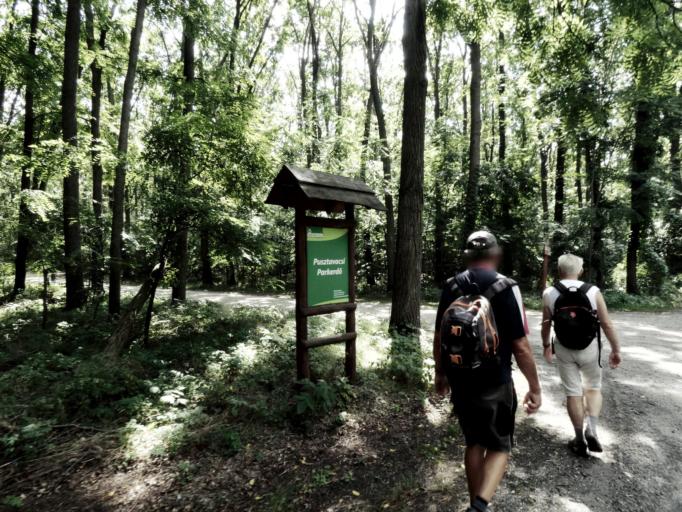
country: HU
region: Pest
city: Hernad
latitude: 47.1596
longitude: 19.4836
